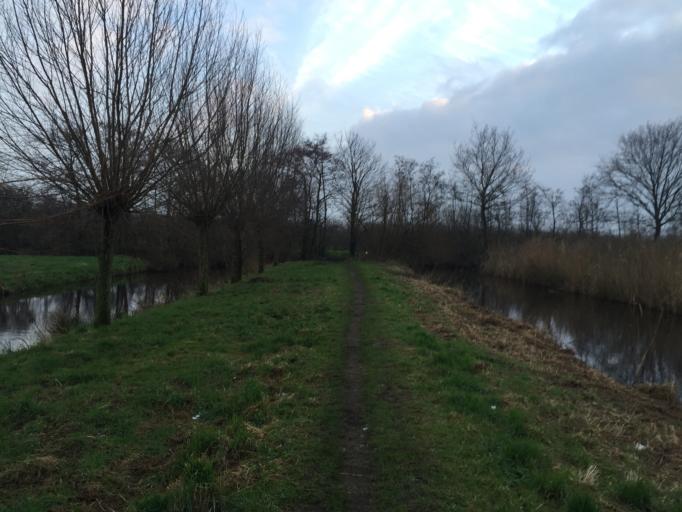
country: NL
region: Utrecht
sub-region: Gemeente Woerden
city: Woerden
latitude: 52.0903
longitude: 4.9252
